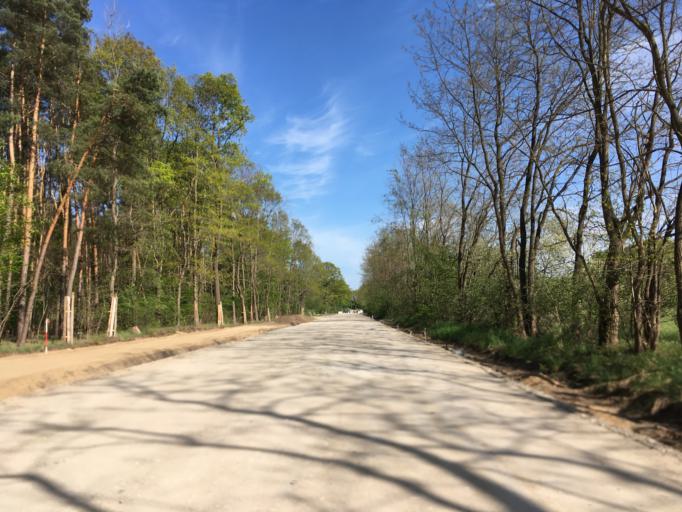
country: DE
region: Brandenburg
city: Rudnitz
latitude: 52.7256
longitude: 13.6096
